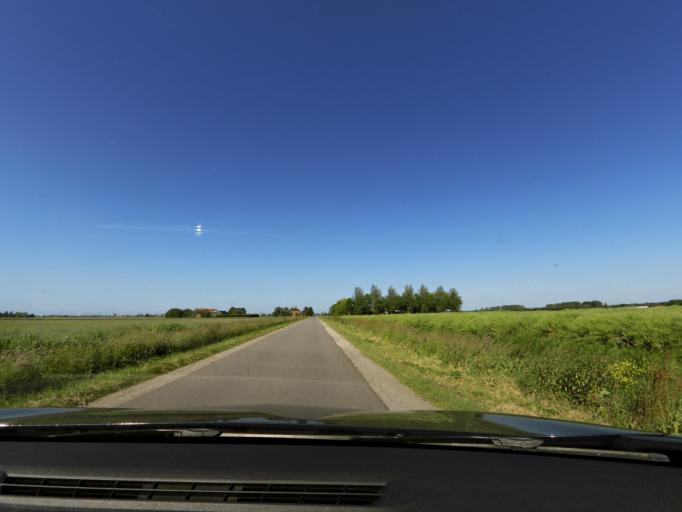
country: NL
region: South Holland
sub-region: Gemeente Hellevoetsluis
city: Nieuwenhoorn
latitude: 51.8600
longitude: 4.1365
